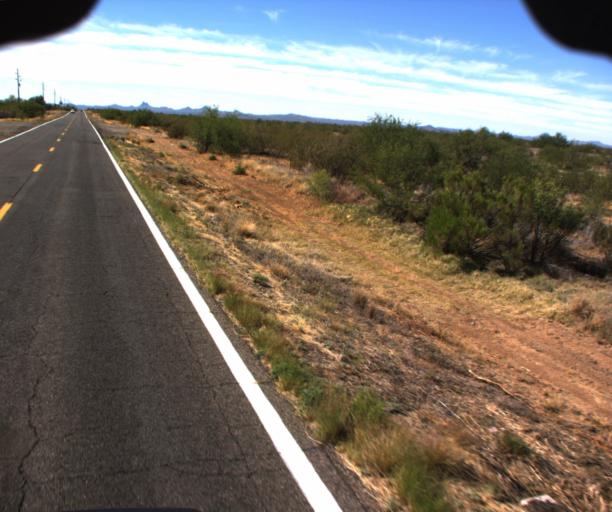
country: US
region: Arizona
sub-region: Yavapai County
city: Congress
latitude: 34.1299
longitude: -112.8388
